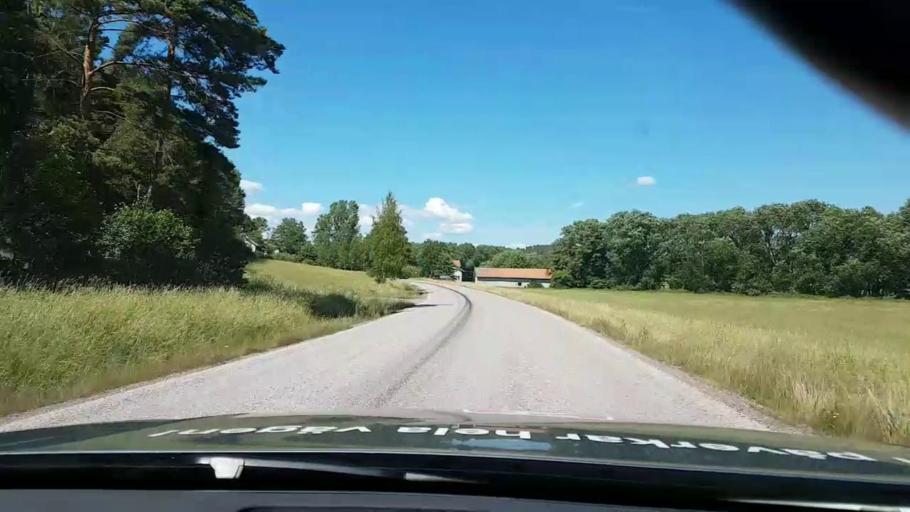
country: SE
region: Kalmar
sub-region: Vasterviks Kommun
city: Forserum
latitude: 57.9481
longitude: 16.4471
